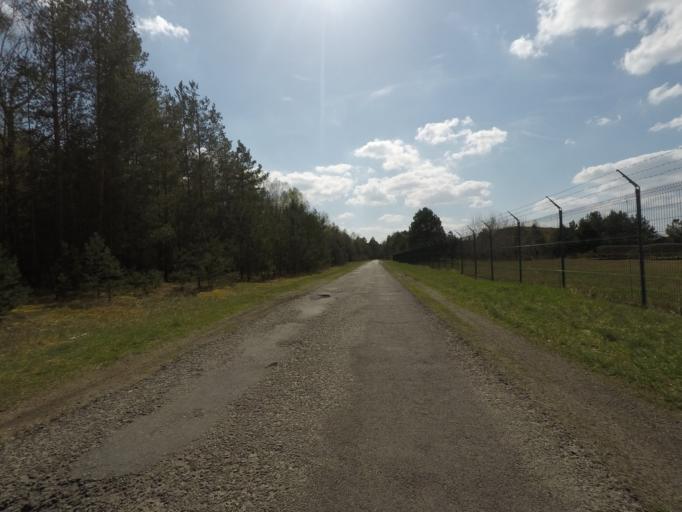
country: DE
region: Brandenburg
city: Melchow
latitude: 52.8221
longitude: 13.7142
